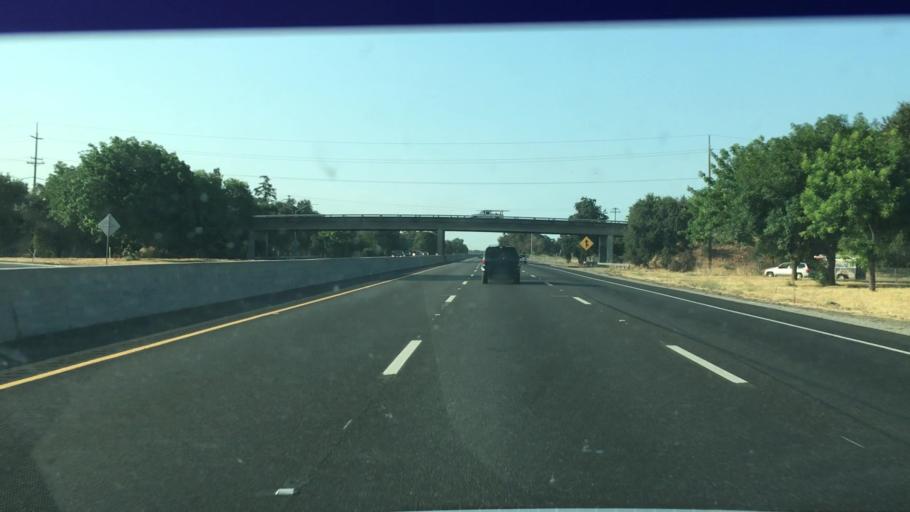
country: US
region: California
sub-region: San Joaquin County
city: Morada
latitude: 38.0386
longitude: -121.2585
